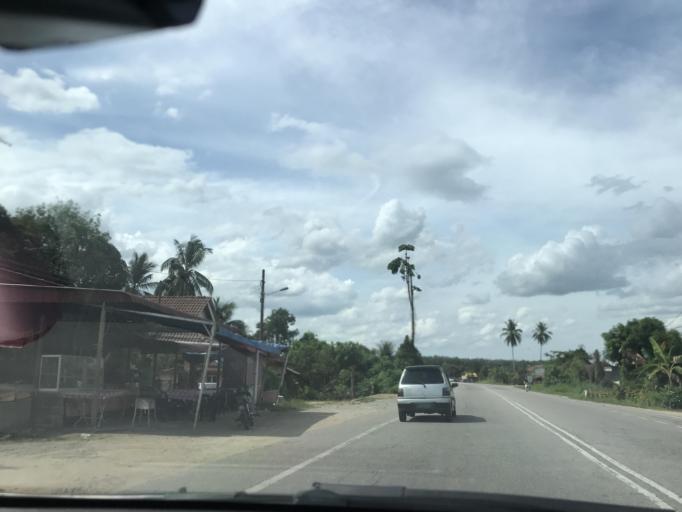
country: MY
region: Kelantan
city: Tanah Merah
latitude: 5.8548
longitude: 102.1669
